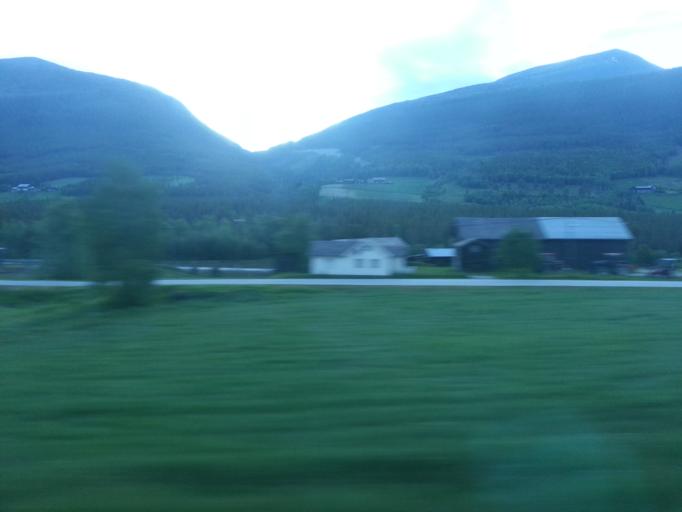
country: NO
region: Oppland
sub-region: Dovre
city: Dovre
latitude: 61.9196
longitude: 9.3373
